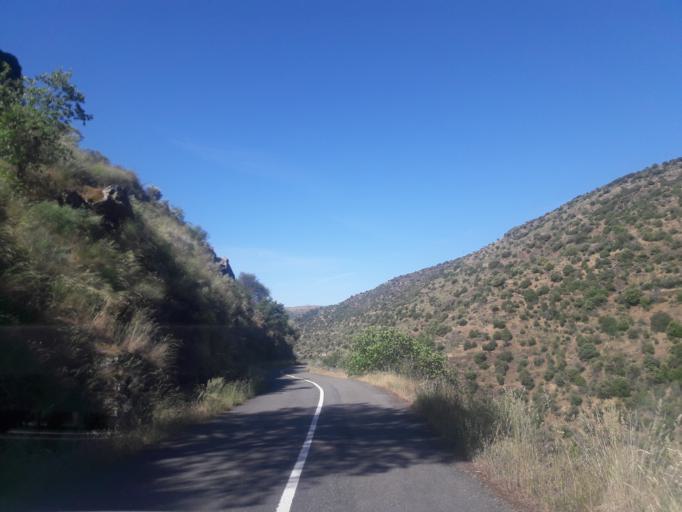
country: ES
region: Castille and Leon
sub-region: Provincia de Salamanca
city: Saucelle
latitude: 41.0362
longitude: -6.7384
